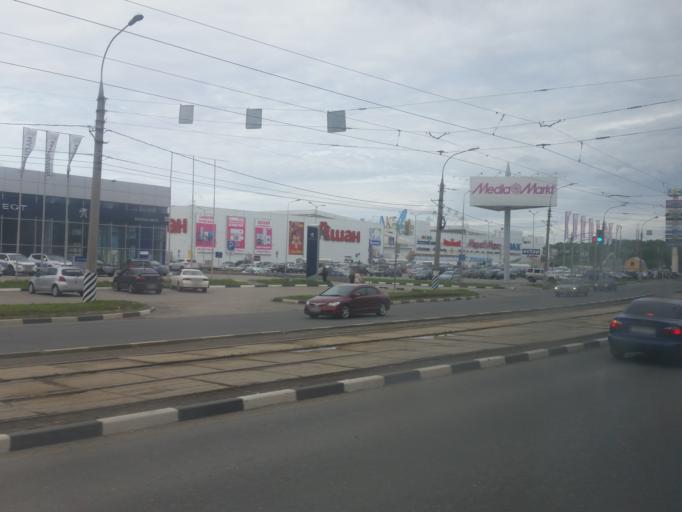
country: RU
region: Ulyanovsk
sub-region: Ulyanovskiy Rayon
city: Ulyanovsk
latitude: 54.3051
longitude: 48.3559
